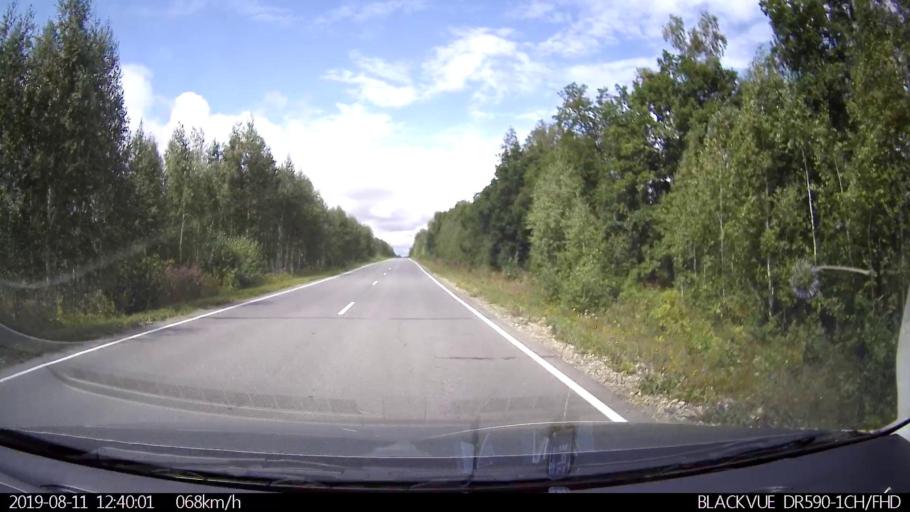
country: RU
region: Ulyanovsk
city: Ignatovka
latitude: 53.8363
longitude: 47.7871
